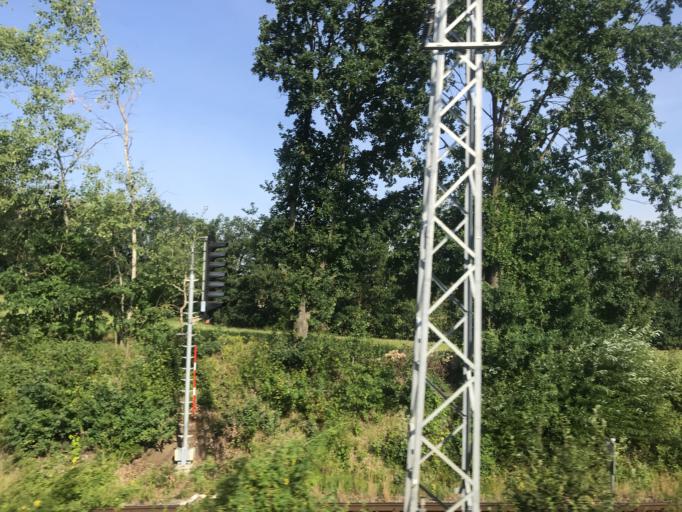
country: CZ
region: Jihocesky
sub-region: Okres Tabor
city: Tabor
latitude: 49.4313
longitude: 14.6659
